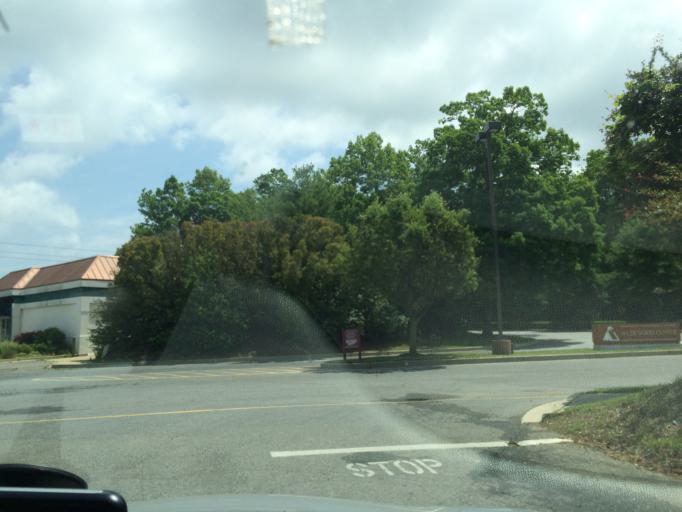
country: US
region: Maryland
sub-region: Saint Mary's County
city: California
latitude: 38.3082
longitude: -76.5320
